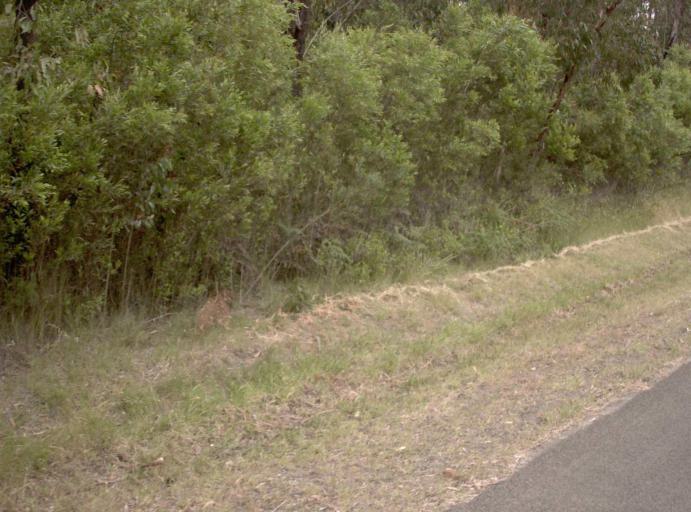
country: AU
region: Victoria
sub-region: Latrobe
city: Moe
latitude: -38.3227
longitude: 146.2599
